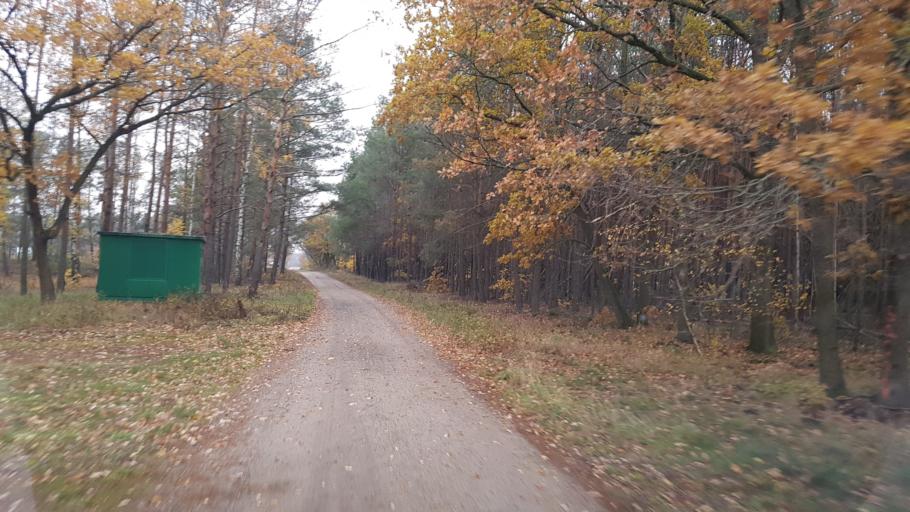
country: DE
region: Brandenburg
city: Schilda
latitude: 51.6391
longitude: 13.3979
